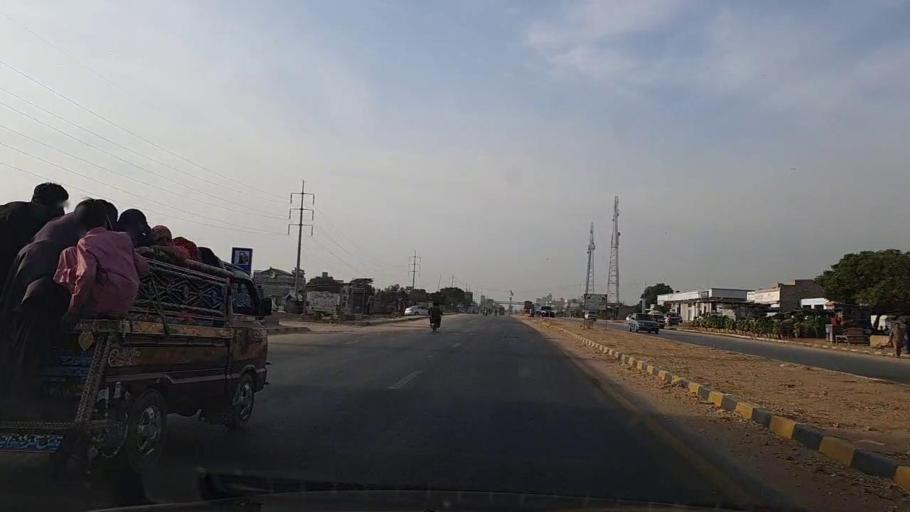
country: PK
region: Sindh
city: Gharo
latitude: 24.7870
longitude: 67.5296
